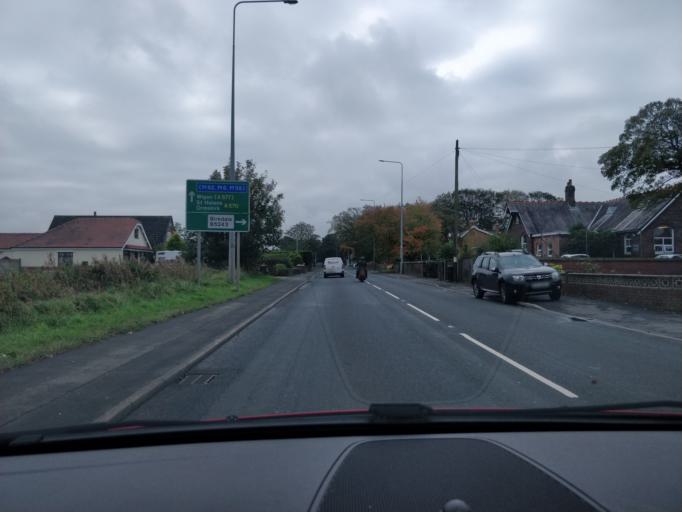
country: GB
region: England
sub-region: Lancashire
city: Banks
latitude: 53.6151
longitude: -2.9402
